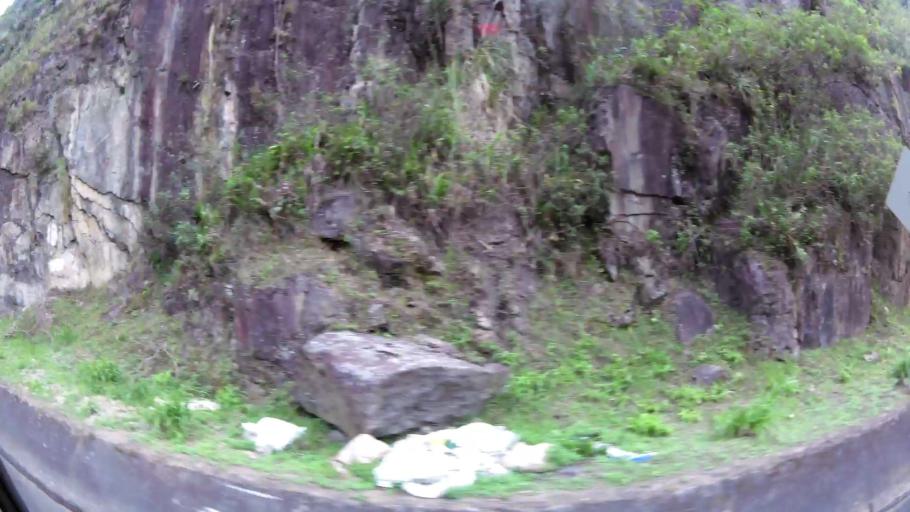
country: EC
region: Tungurahua
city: Banos
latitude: -1.3991
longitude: -78.3807
